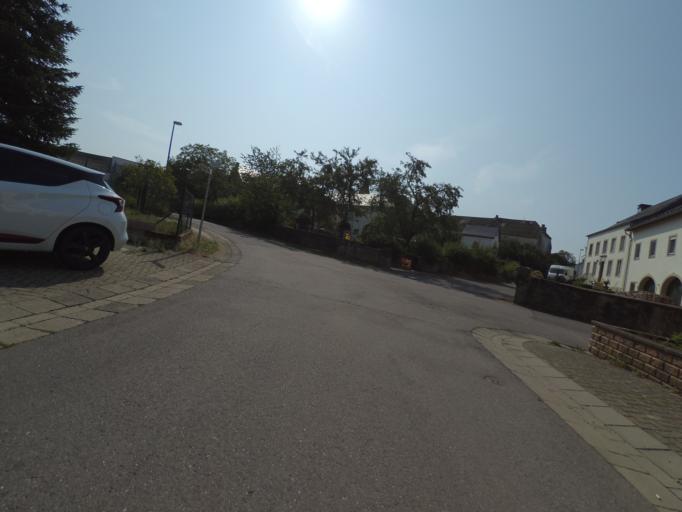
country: DE
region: Saarland
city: Perl
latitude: 49.4771
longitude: 6.4450
